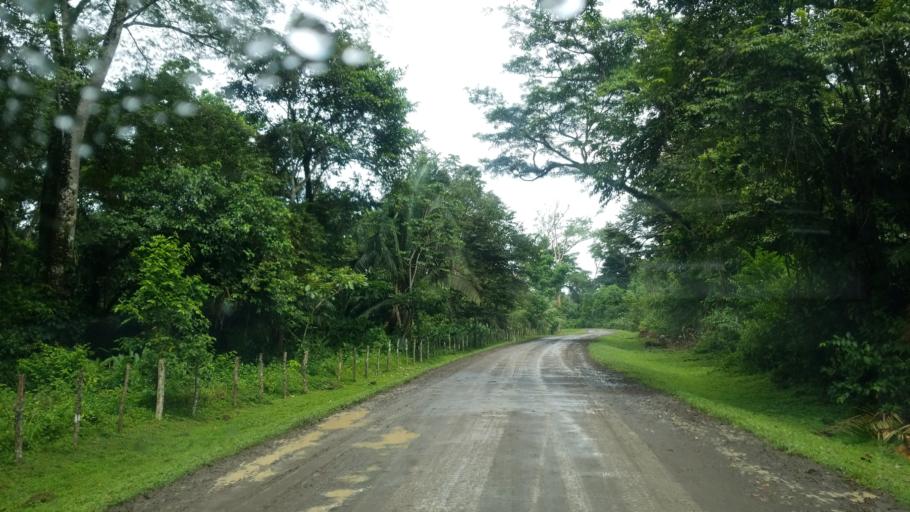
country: CR
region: Alajuela
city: San Jose
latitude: 11.0845
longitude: -85.2363
